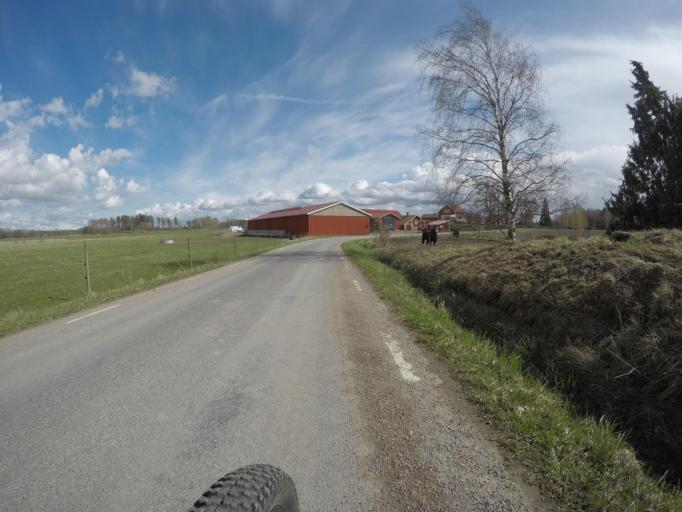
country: SE
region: Vaestmanland
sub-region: Kungsors Kommun
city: Kungsoer
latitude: 59.2986
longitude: 16.1406
